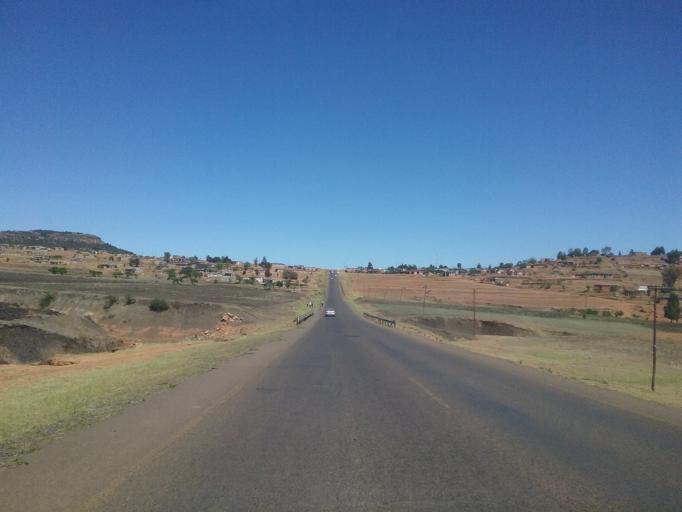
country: LS
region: Quthing
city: Quthing
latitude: -30.3962
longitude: 27.6460
